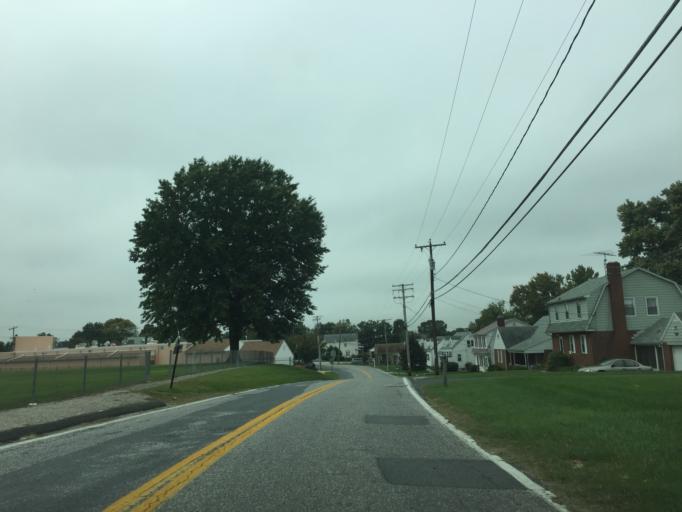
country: US
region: Maryland
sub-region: Baltimore County
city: Rosedale
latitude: 39.3329
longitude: -76.4995
